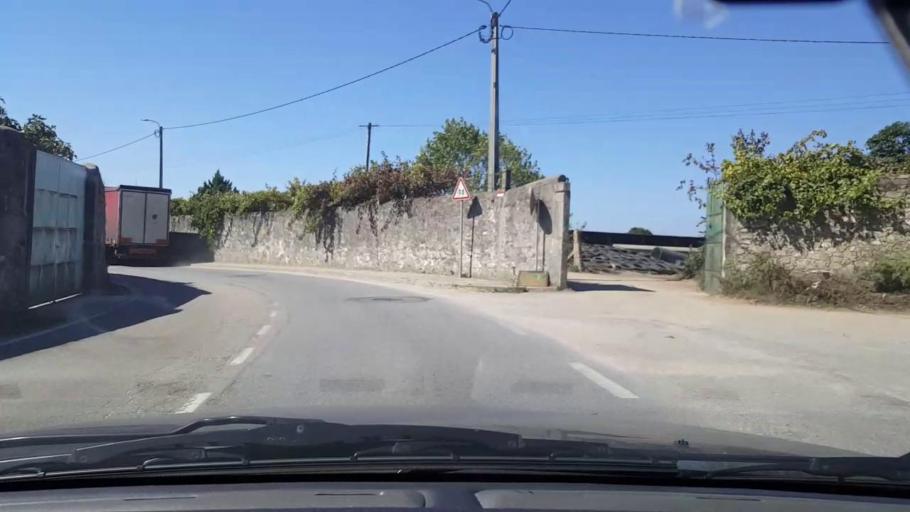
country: PT
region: Porto
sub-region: Vila do Conde
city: Arvore
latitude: 41.3411
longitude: -8.6986
